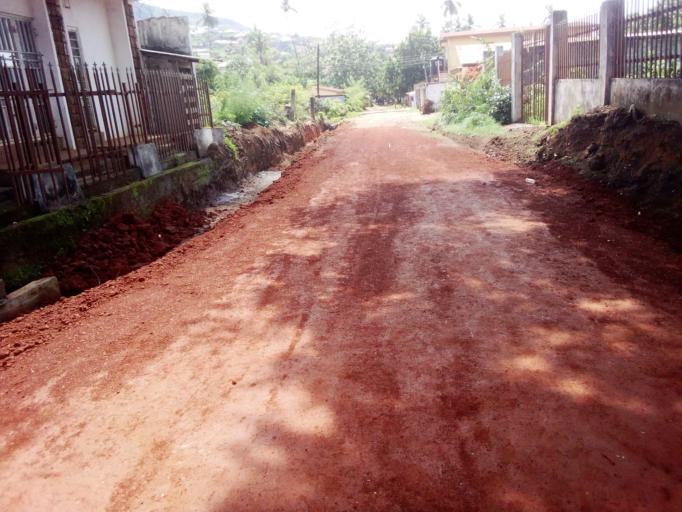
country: SL
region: Western Area
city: Waterloo
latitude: 8.3392
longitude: -13.0718
